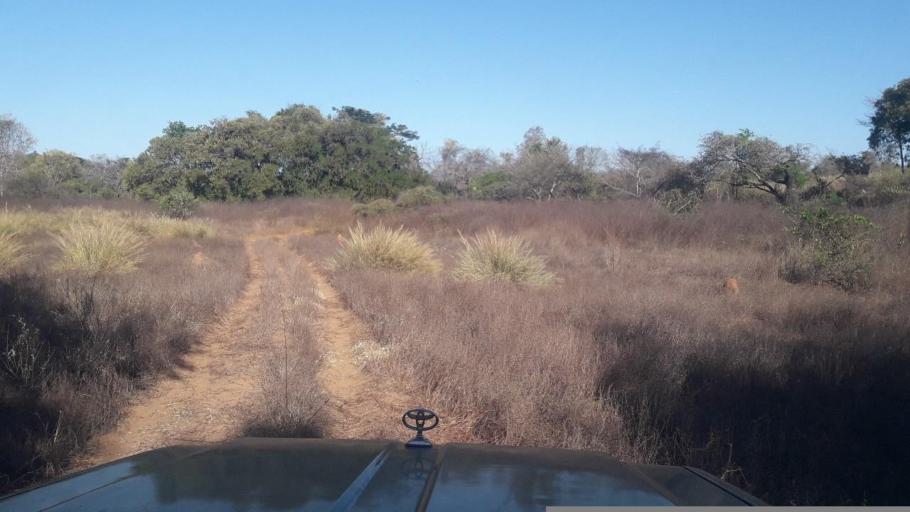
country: MG
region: Boeny
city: Sitampiky
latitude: -16.4233
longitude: 45.6195
